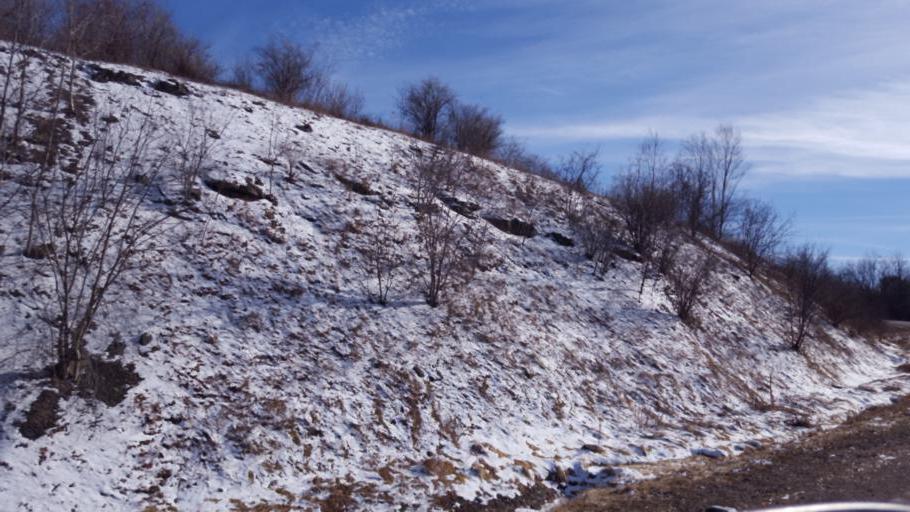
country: US
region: New York
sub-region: Allegany County
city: Wellsville
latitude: 42.1189
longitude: -77.9948
